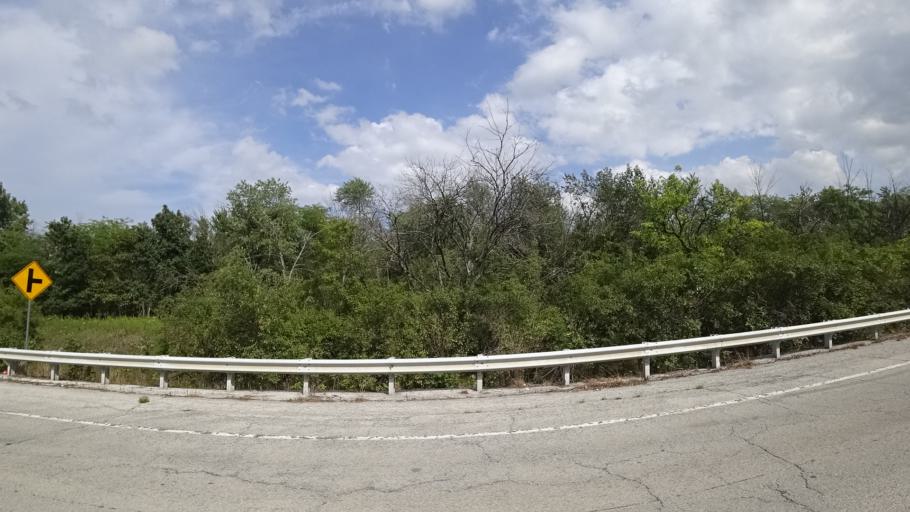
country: US
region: Illinois
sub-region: Cook County
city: Tinley Park
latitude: 41.5403
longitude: -87.7711
